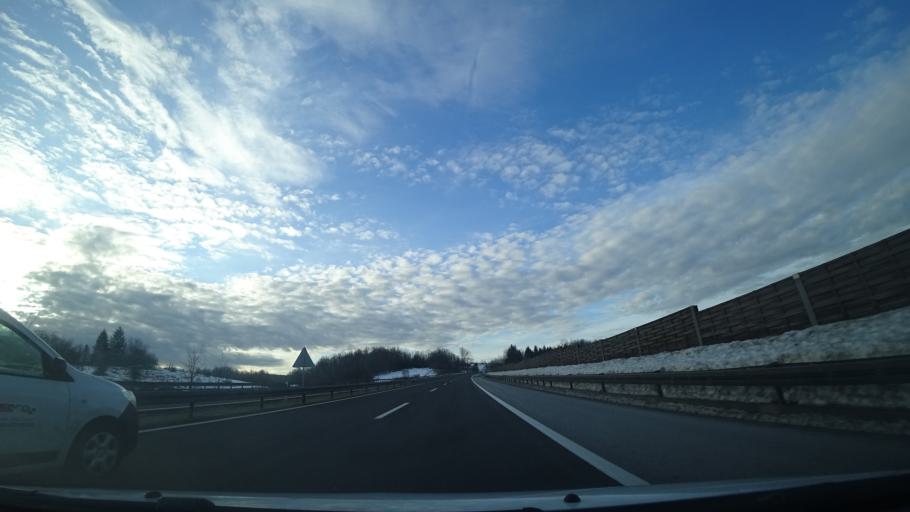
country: HR
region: Karlovacka
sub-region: Grad Ogulin
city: Ogulin
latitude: 45.3230
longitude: 15.2825
